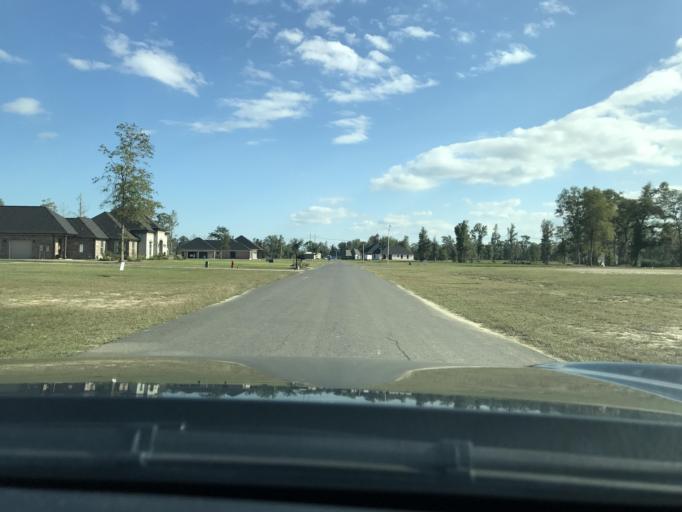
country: US
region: Louisiana
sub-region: Calcasieu Parish
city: Moss Bluff
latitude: 30.3356
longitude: -93.2507
